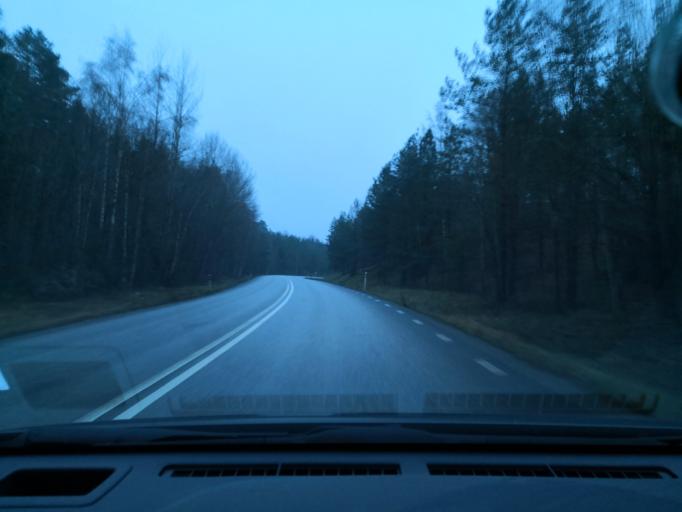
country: SE
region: Soedermanland
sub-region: Eskilstuna Kommun
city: Skogstorp
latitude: 59.3065
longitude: 16.4485
